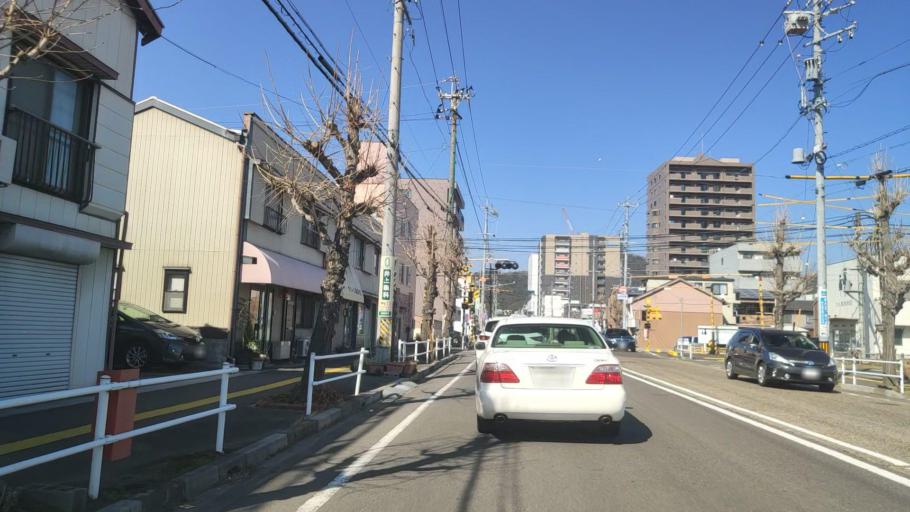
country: JP
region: Gifu
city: Gifu-shi
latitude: 35.4105
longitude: 136.7672
